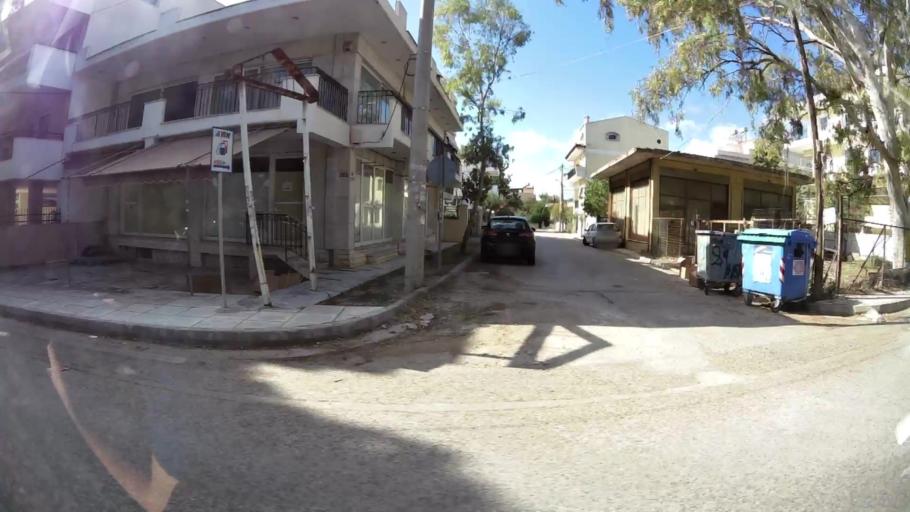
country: GR
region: Attica
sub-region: Nomarchia Anatolikis Attikis
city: Acharnes
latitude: 38.0986
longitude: 23.7377
